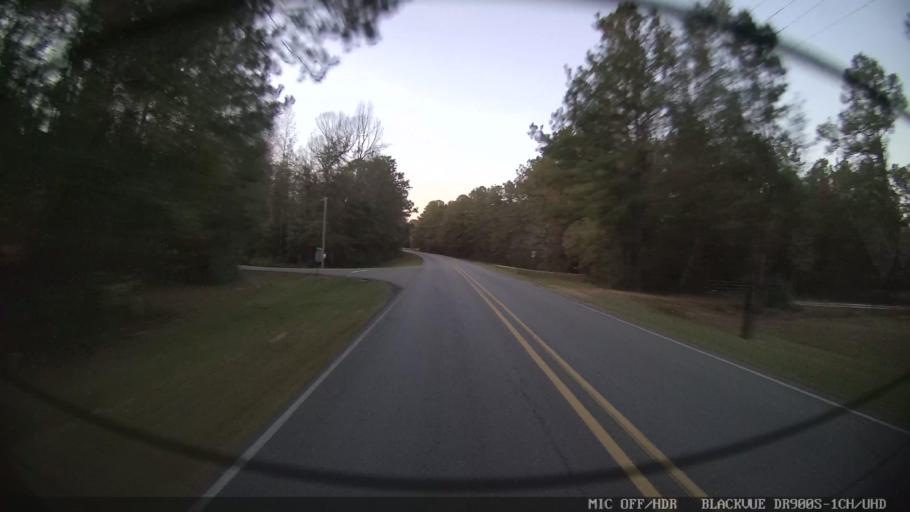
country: US
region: Mississippi
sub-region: Perry County
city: New Augusta
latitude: 31.0653
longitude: -89.1909
